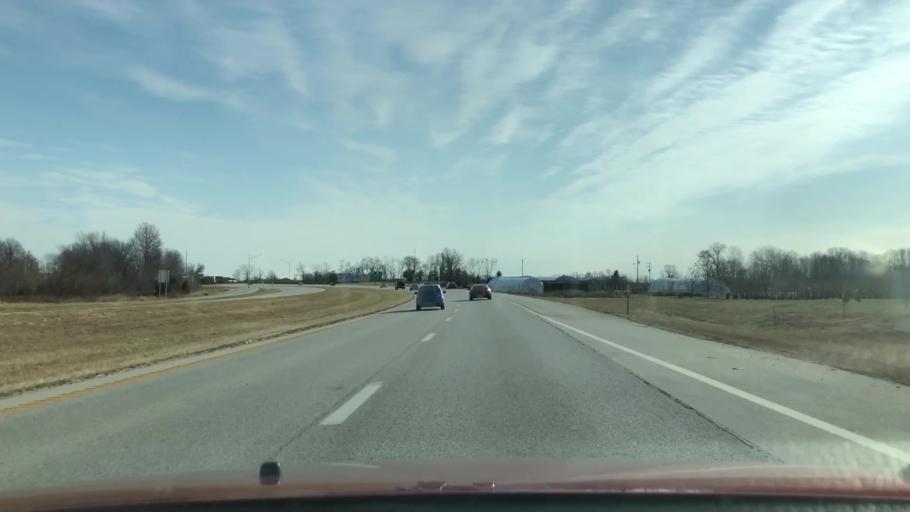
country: US
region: Missouri
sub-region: Webster County
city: Rogersville
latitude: 37.1105
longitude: -93.0679
